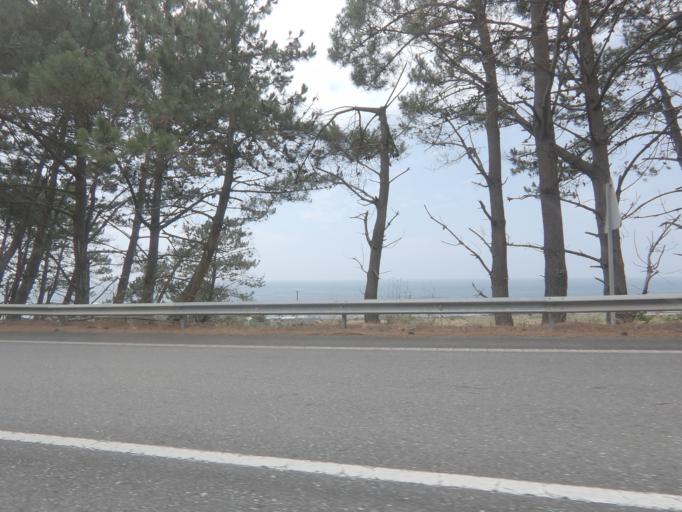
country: ES
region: Galicia
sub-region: Provincia de Pontevedra
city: Oia
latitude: 41.9558
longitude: -8.8835
